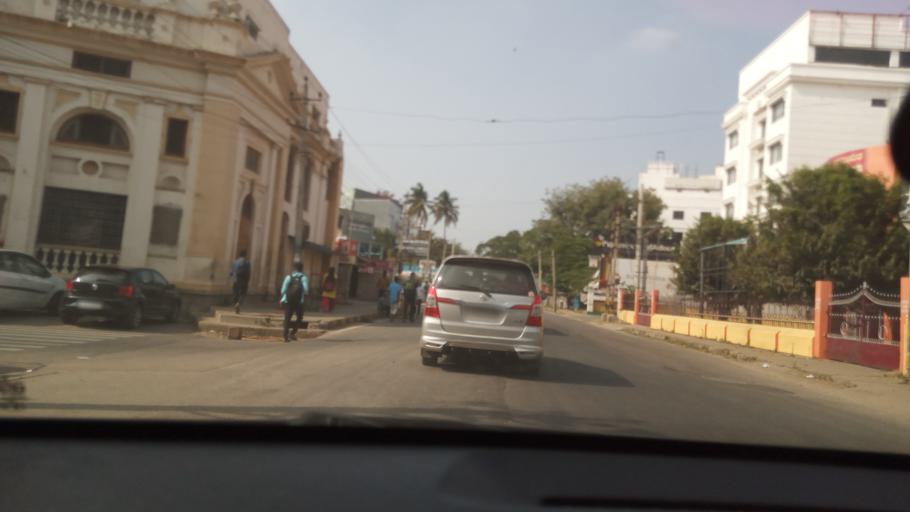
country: IN
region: Karnataka
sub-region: Mysore
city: Mysore
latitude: 12.3084
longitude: 76.6595
